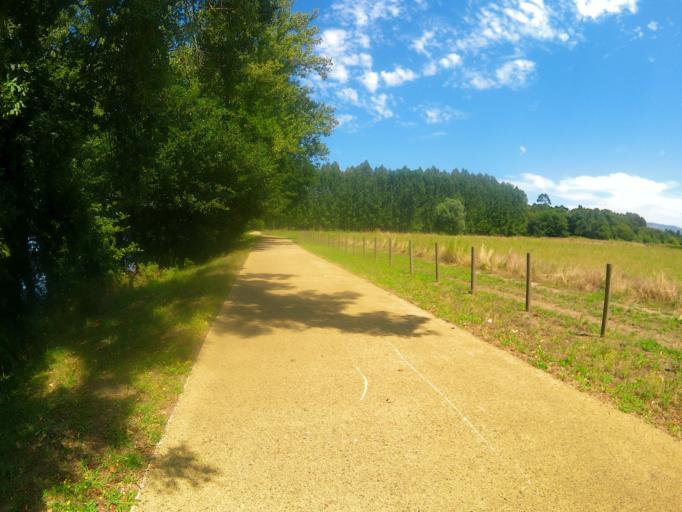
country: ES
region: Galicia
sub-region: Provincia de Pontevedra
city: Tomino
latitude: 41.9846
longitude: -8.6936
